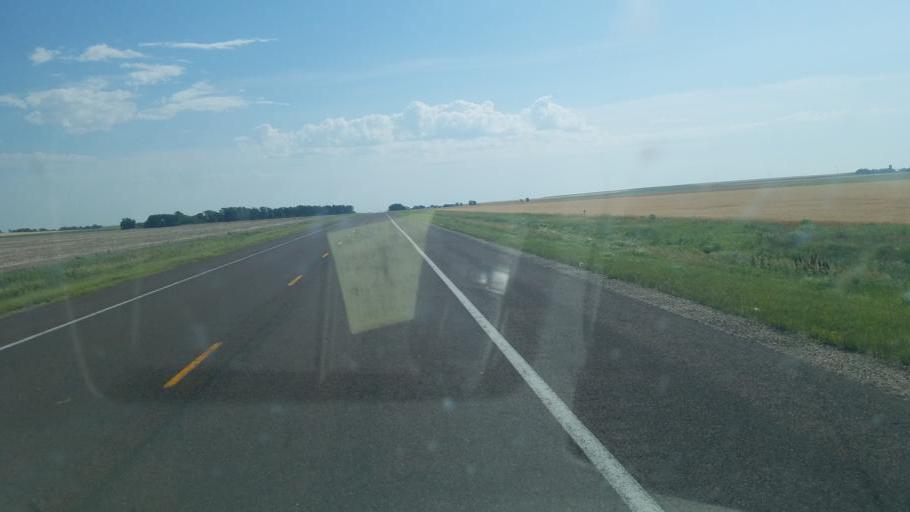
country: US
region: Kansas
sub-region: Ellsworth County
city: Ellsworth
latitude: 38.6242
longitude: -98.3642
